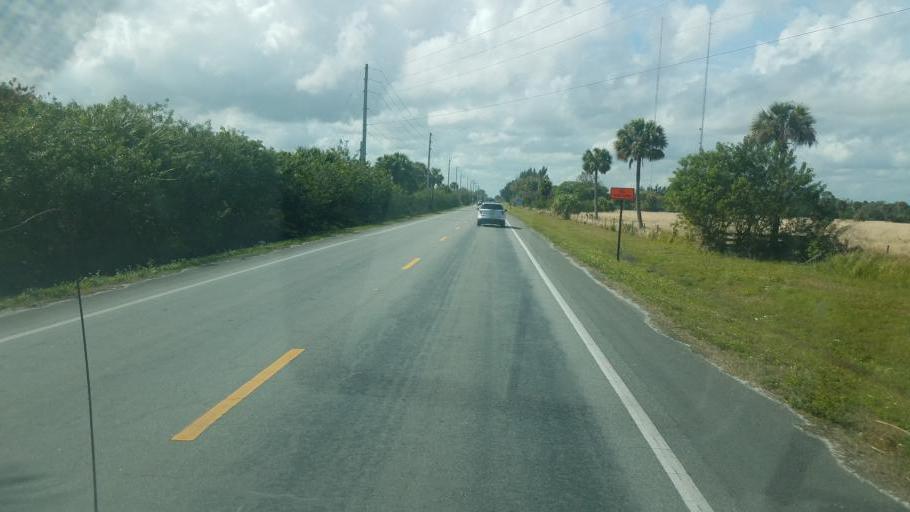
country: US
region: Florida
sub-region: Saint Lucie County
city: Lakewood Park
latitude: 27.4475
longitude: -80.4031
